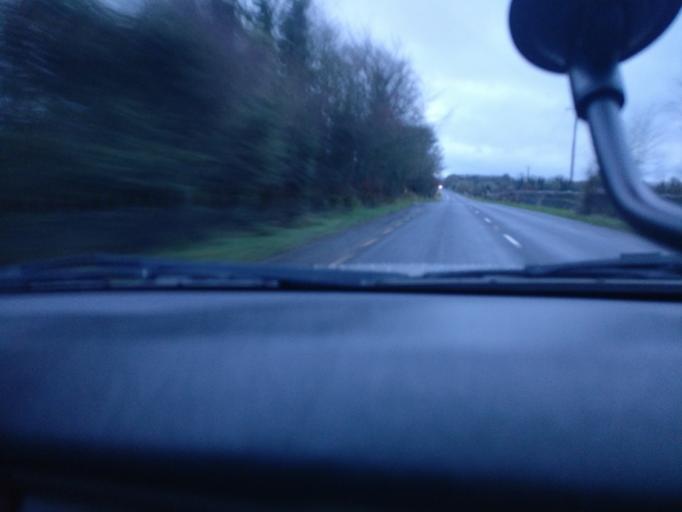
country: IE
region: Connaught
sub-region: County Galway
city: Loughrea
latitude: 53.2553
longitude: -8.4396
